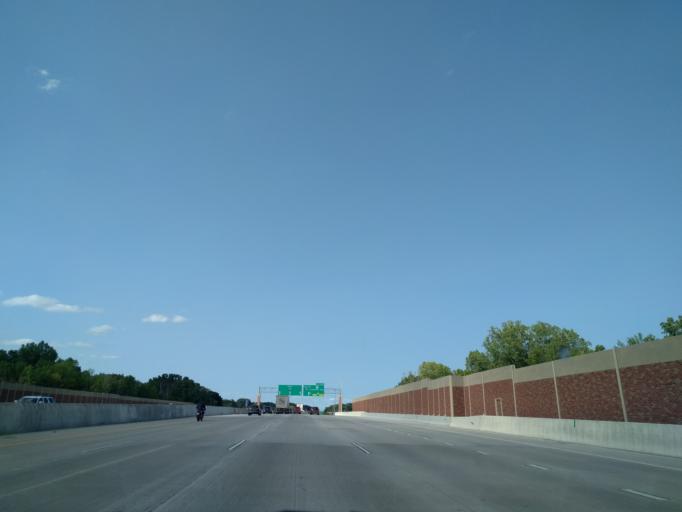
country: US
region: Wisconsin
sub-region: Brown County
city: Ashwaubenon
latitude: 44.5025
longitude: -88.0819
